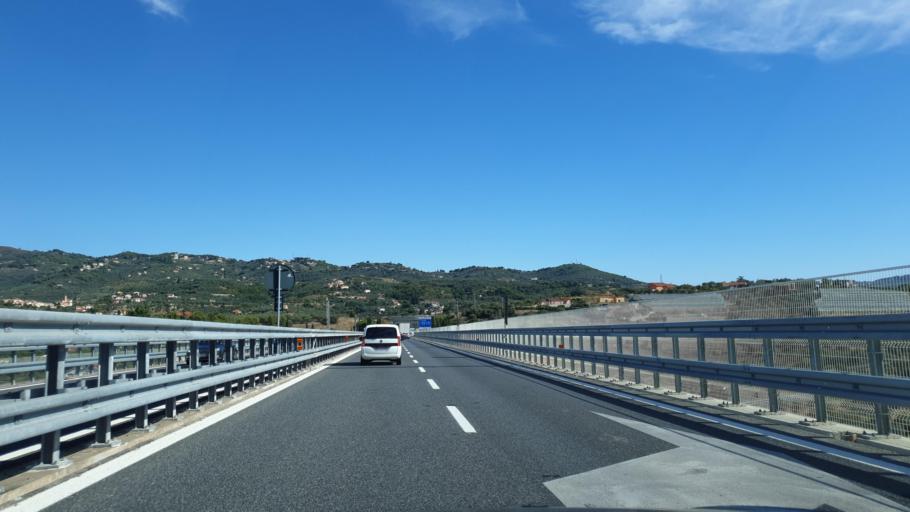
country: IT
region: Liguria
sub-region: Provincia di Imperia
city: San Lorenzo al Mare
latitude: 43.8741
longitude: 7.9937
